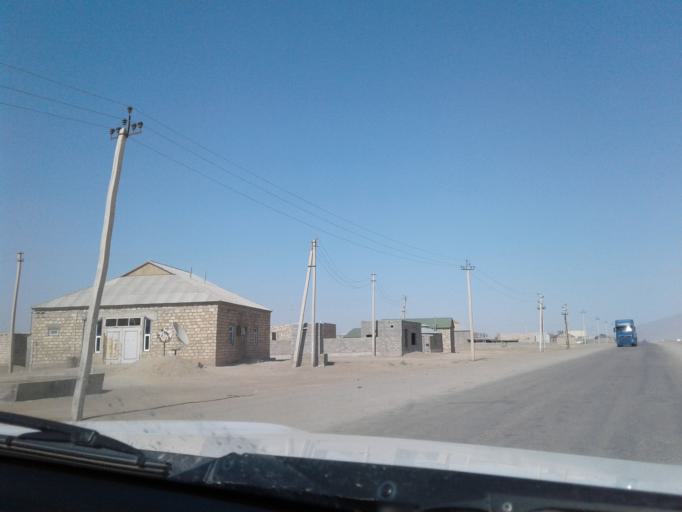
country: TM
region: Balkan
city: Gumdag
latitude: 39.2018
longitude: 54.6108
